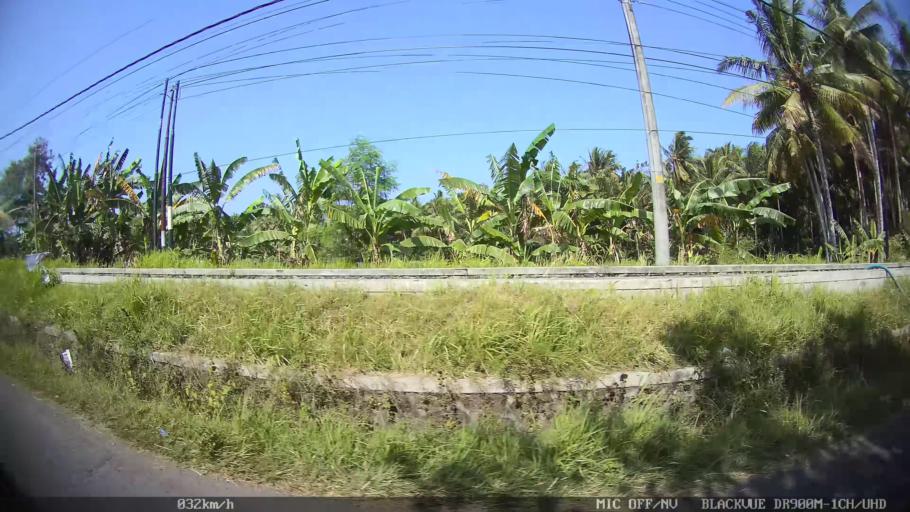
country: ID
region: Daerah Istimewa Yogyakarta
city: Srandakan
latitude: -7.9221
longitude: 110.1851
